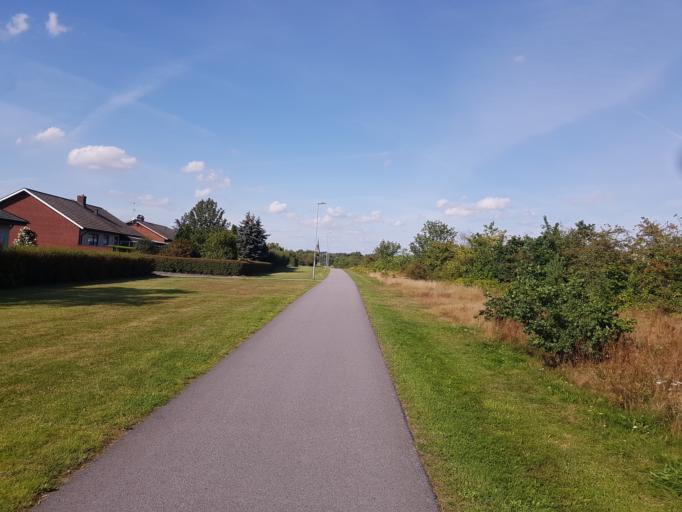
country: SE
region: Skane
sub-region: Sjobo Kommun
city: Sjoebo
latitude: 55.6370
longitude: 13.6991
